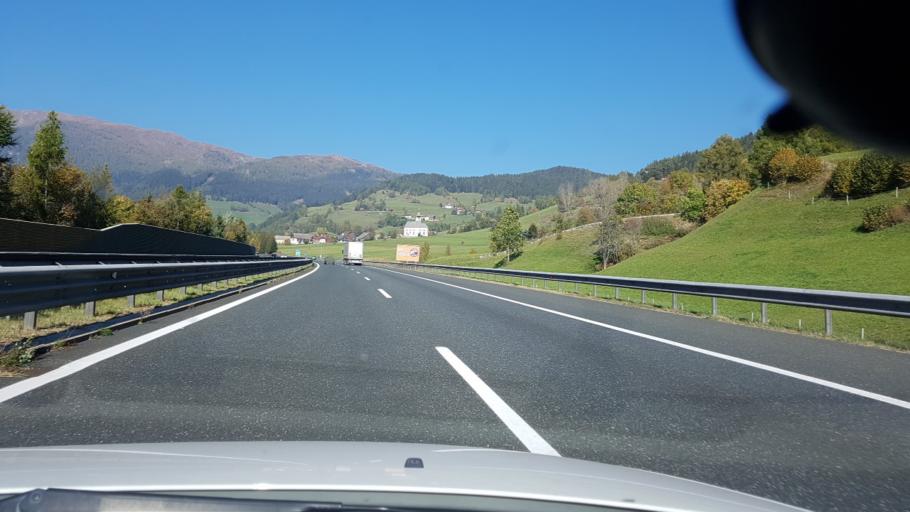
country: AT
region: Salzburg
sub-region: Politischer Bezirk Tamsweg
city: Sankt Michael im Lungau
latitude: 47.0151
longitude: 13.6174
